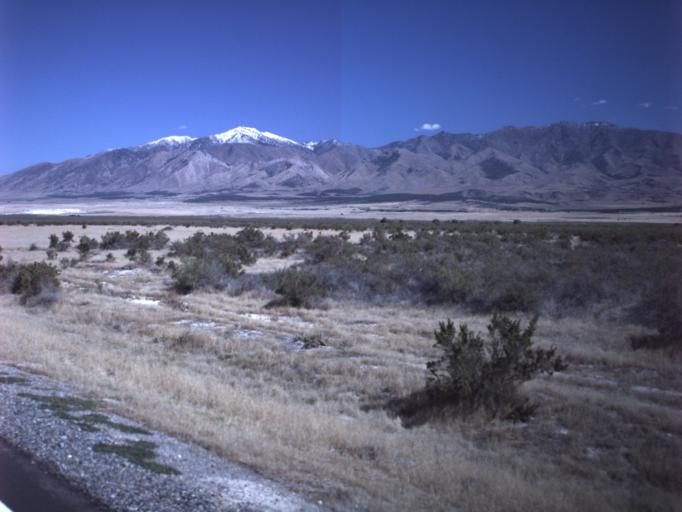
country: US
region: Utah
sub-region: Tooele County
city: Grantsville
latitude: 40.2989
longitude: -112.7427
